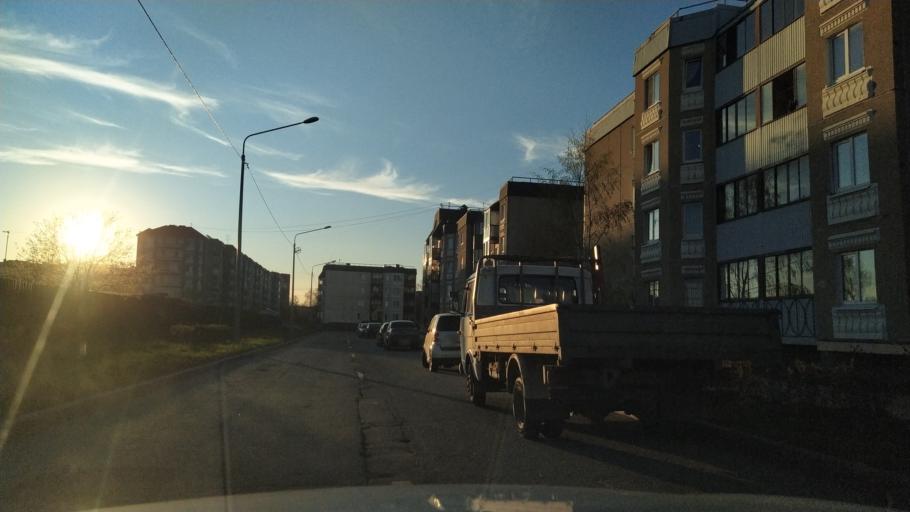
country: RU
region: St.-Petersburg
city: Pushkin
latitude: 59.7028
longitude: 30.3791
